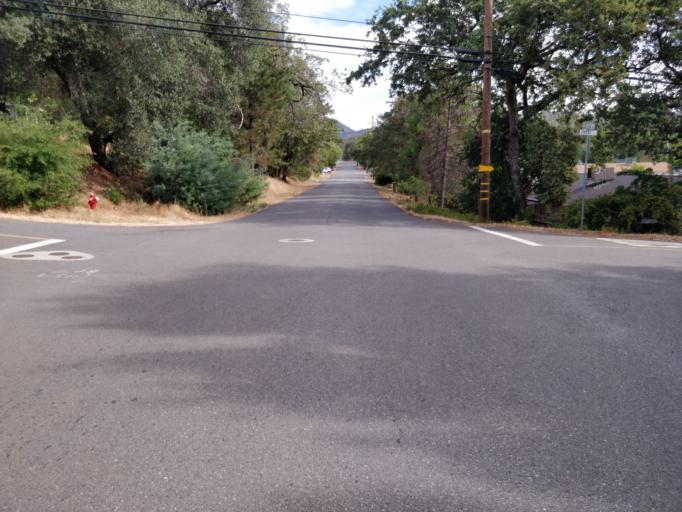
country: US
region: California
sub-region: Shasta County
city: Shasta Lake
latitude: 40.6809
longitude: -122.3567
